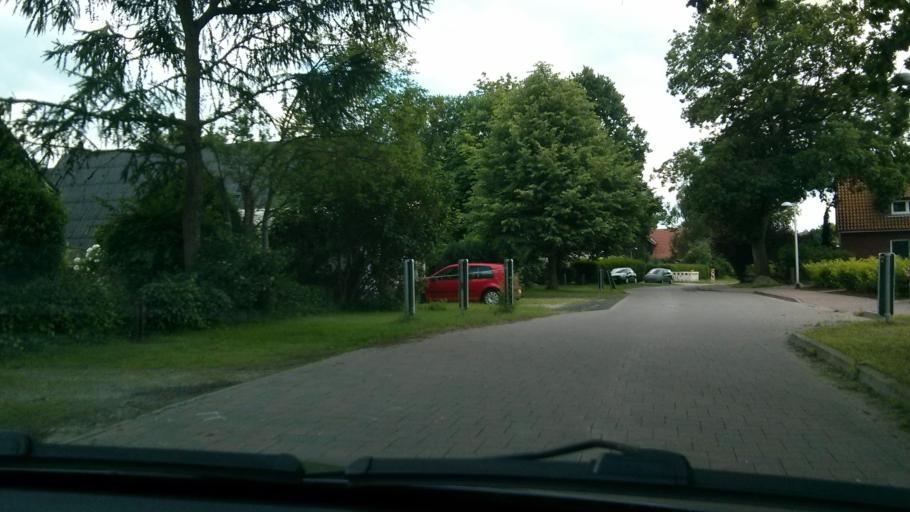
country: DE
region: Lower Saxony
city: Loxstedt
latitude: 53.4934
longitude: 8.6884
